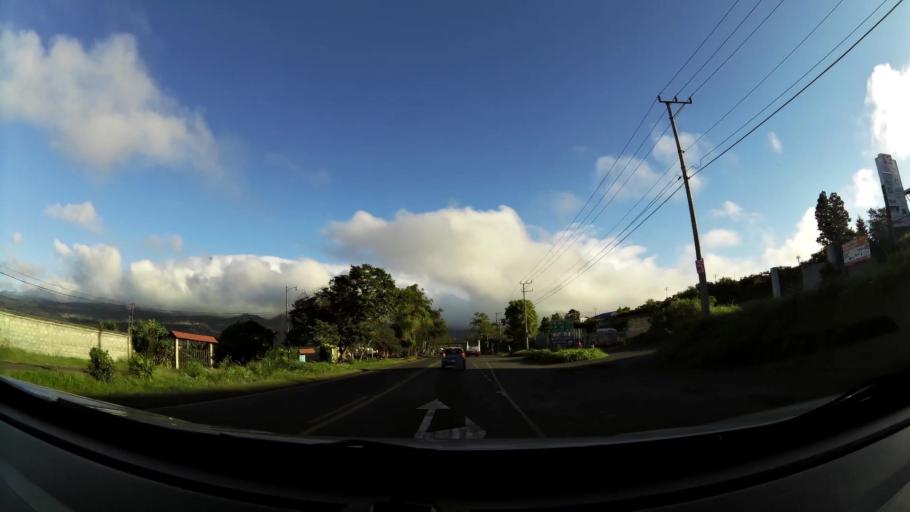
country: CR
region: Heredia
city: Angeles
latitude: 10.0064
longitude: -84.0322
